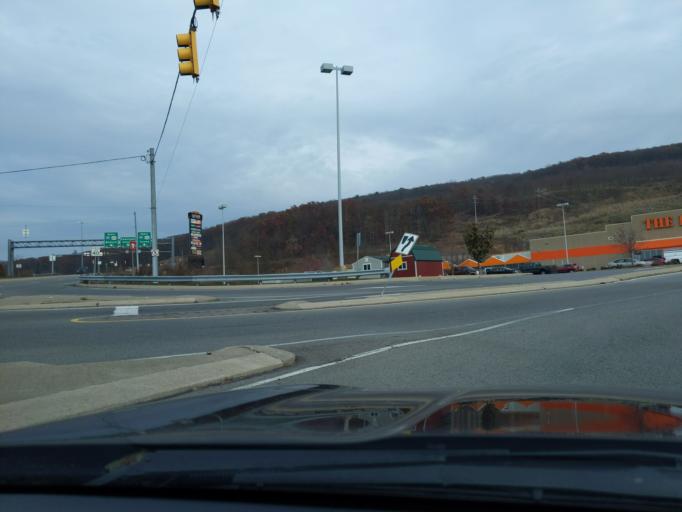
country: US
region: Pennsylvania
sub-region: Blair County
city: Lakemont
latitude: 40.4903
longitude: -78.3843
